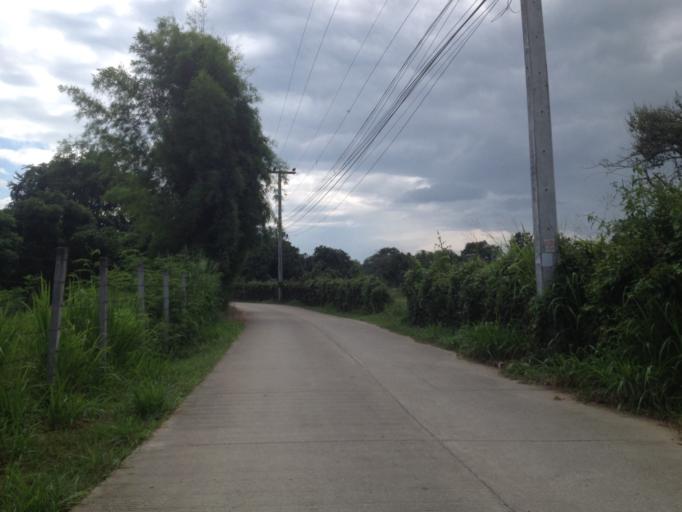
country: TH
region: Chiang Mai
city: Hang Dong
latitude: 18.6856
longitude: 98.8828
